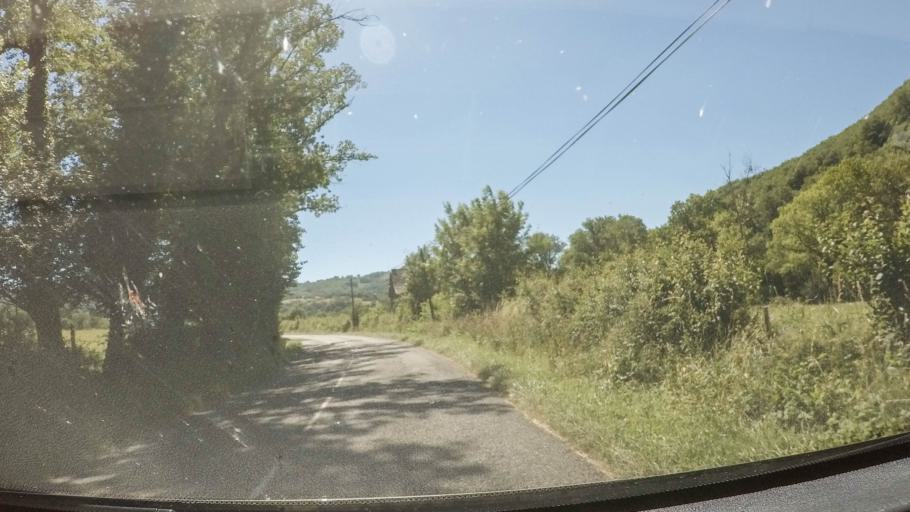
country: FR
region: Midi-Pyrenees
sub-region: Departement de l'Aveyron
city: Saint-Christophe-Vallon
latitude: 44.4640
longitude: 2.3996
